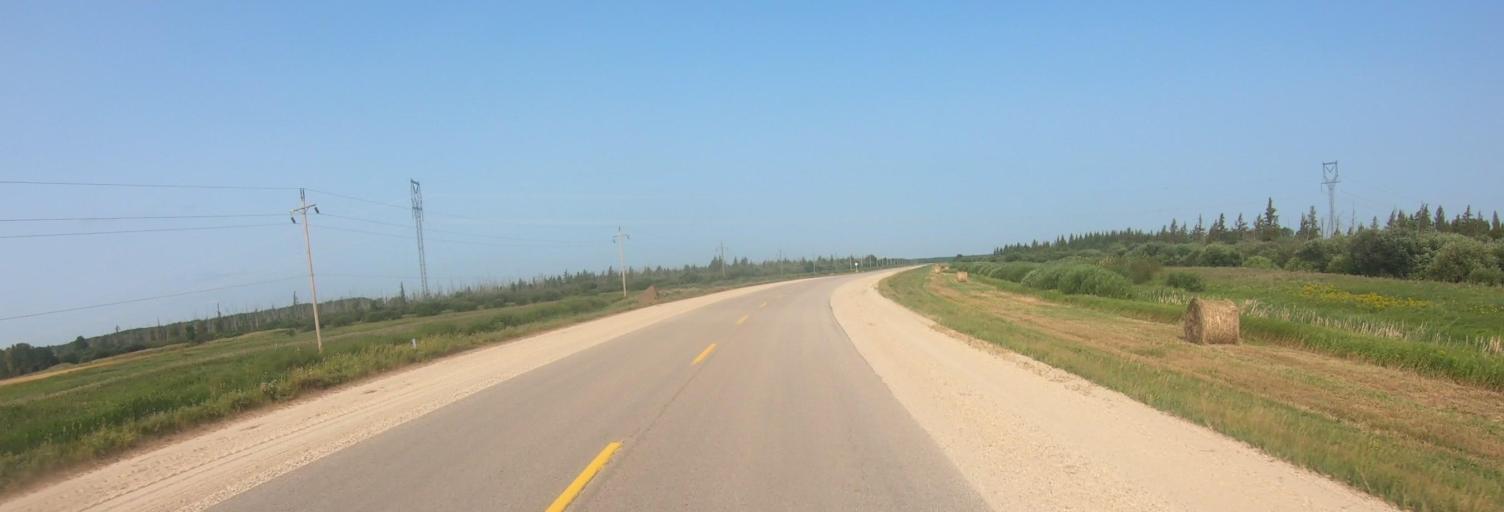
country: US
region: Minnesota
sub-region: Roseau County
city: Warroad
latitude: 49.0159
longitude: -95.5362
